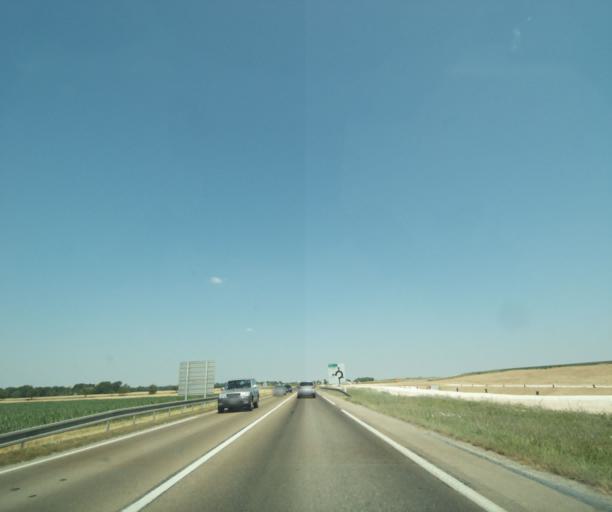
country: FR
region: Champagne-Ardenne
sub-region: Departement de la Marne
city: Sarry
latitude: 48.8870
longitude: 4.4563
